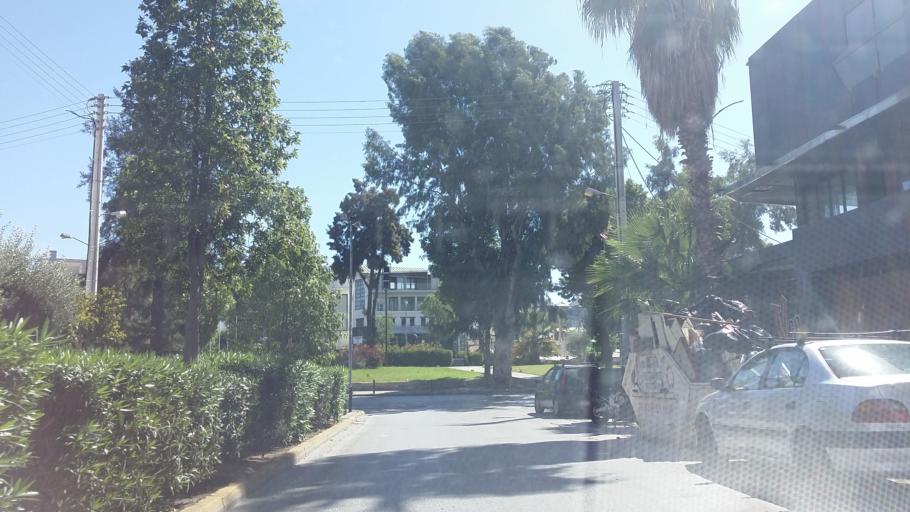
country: GR
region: Attica
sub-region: Nomarchia Athinas
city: Peristeri
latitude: 38.0133
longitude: 23.7063
